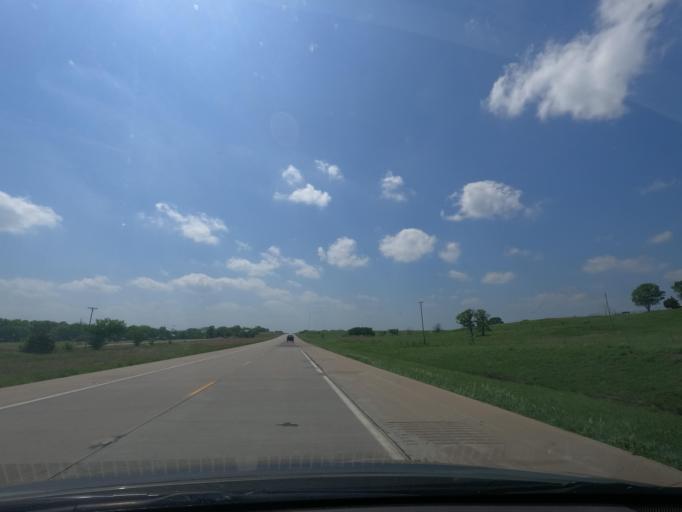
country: US
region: Kansas
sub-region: Elk County
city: Howard
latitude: 37.6275
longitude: -96.0797
